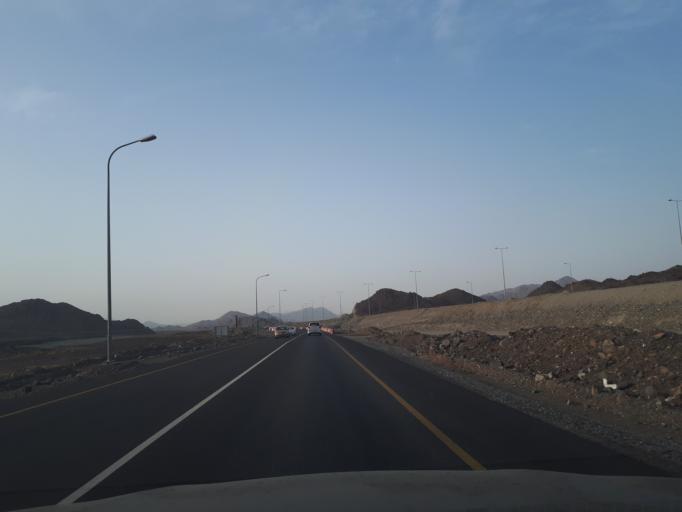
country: OM
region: Muhafazat ad Dakhiliyah
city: Sufalat Sama'il
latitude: 23.2670
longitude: 58.1040
